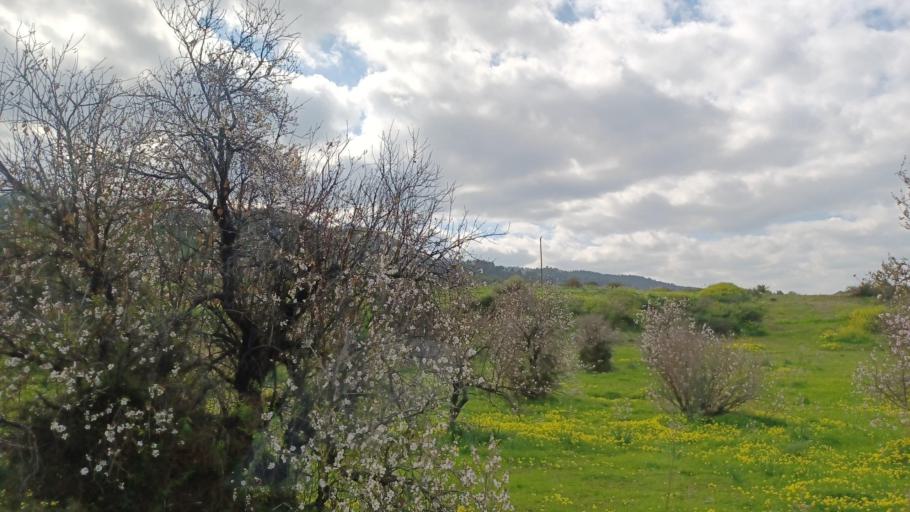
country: CY
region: Pafos
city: Polis
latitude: 35.1032
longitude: 32.5144
